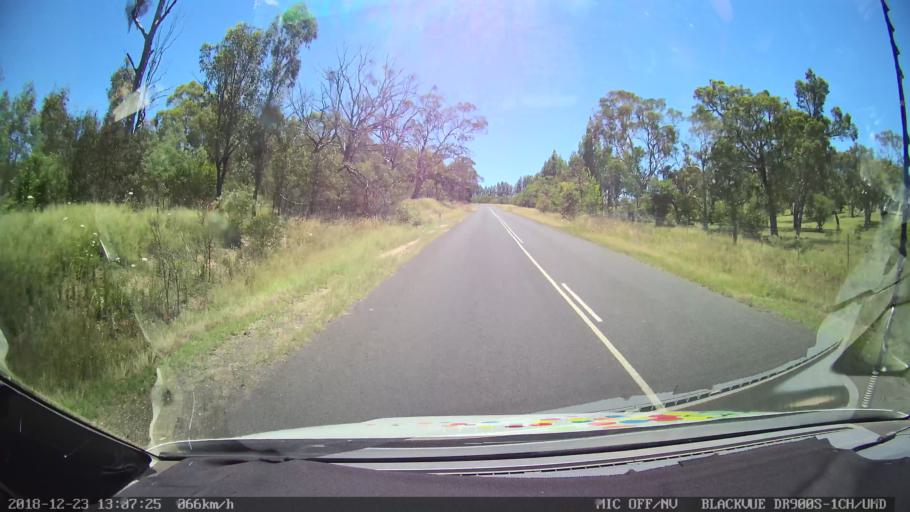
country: AU
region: New South Wales
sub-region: Armidale Dumaresq
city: Armidale
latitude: -30.5156
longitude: 151.6292
